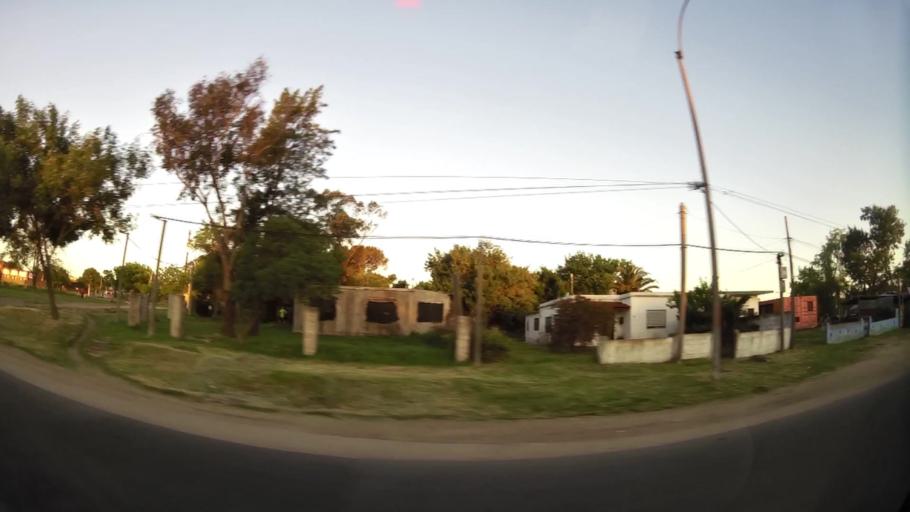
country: UY
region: Montevideo
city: Montevideo
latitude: -34.8246
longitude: -56.1687
